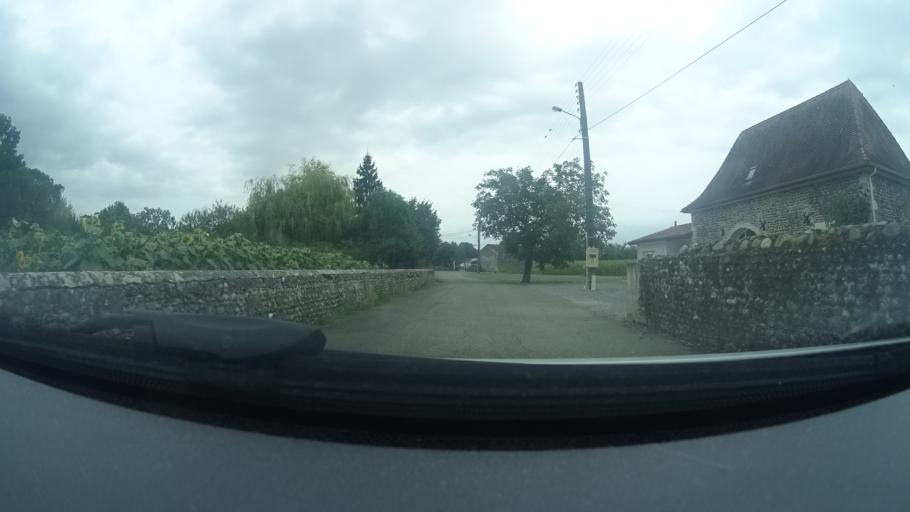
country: FR
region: Aquitaine
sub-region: Departement des Pyrenees-Atlantiques
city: Mont
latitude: 43.4534
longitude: -0.7120
